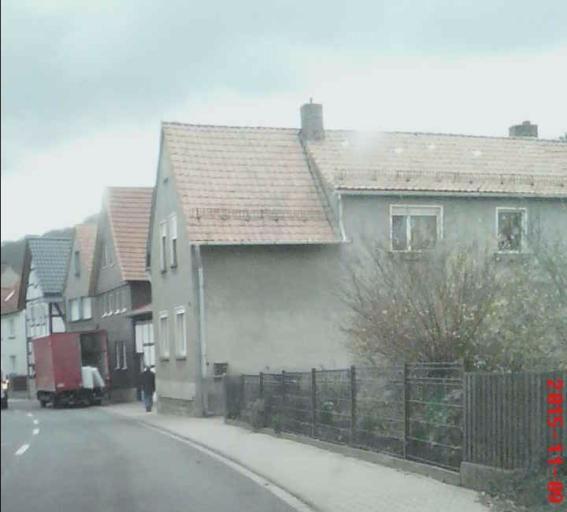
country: DE
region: Thuringia
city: Effelder
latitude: 51.2145
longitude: 10.2199
